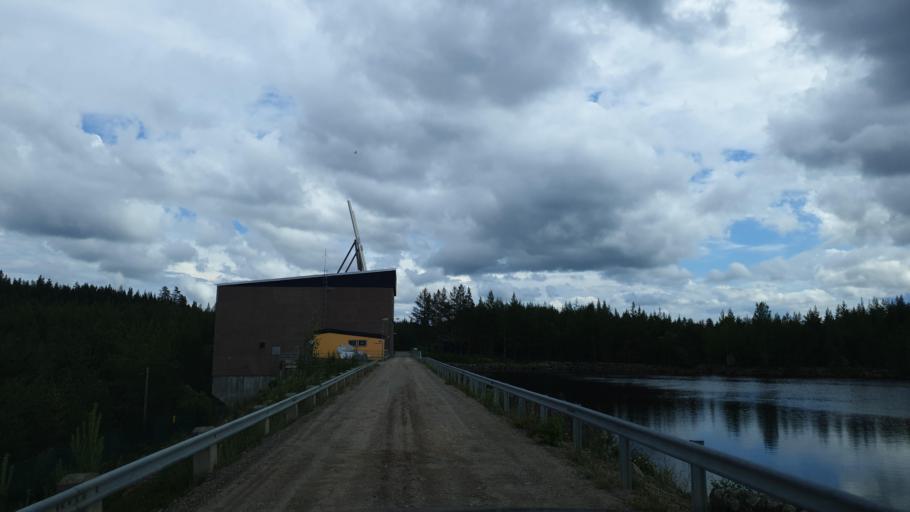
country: SE
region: Jaemtland
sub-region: Harjedalens Kommun
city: Sveg
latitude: 62.0425
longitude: 14.4946
